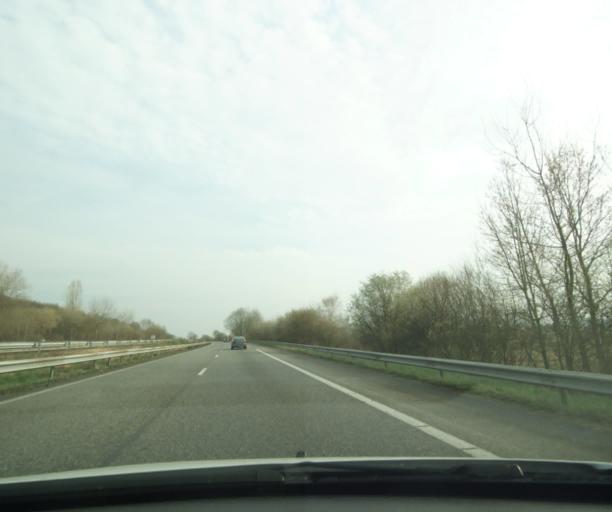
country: FR
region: Aquitaine
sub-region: Departement des Pyrenees-Atlantiques
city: Poey-de-Lescar
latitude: 43.3661
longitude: -0.4794
